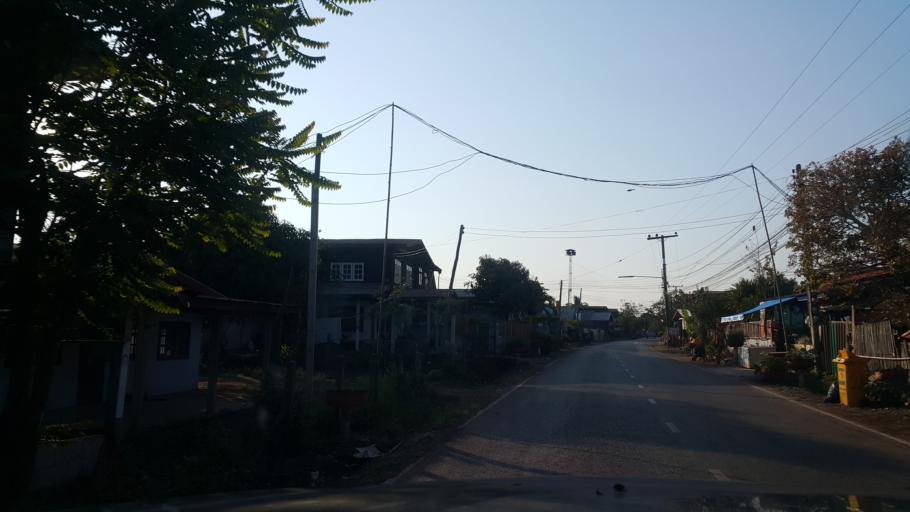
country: TH
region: Changwat Udon Thani
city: Ban Na Muang
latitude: 17.2851
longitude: 102.9618
